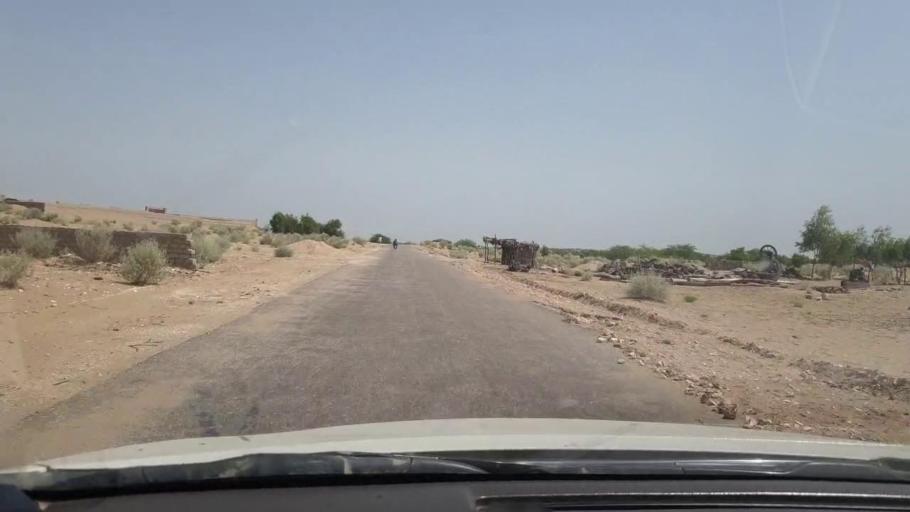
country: PK
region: Sindh
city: Rohri
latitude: 27.4913
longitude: 69.0508
